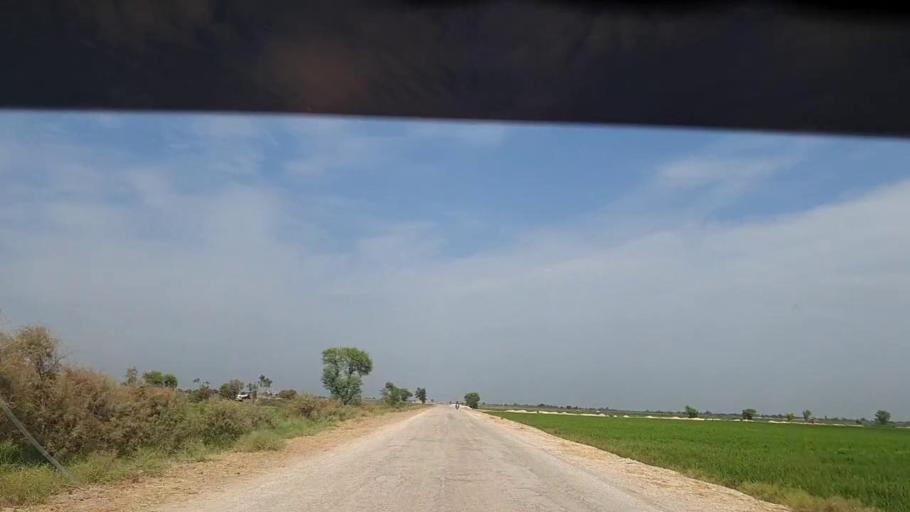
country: PK
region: Sindh
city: Thul
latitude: 28.1945
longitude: 68.7755
